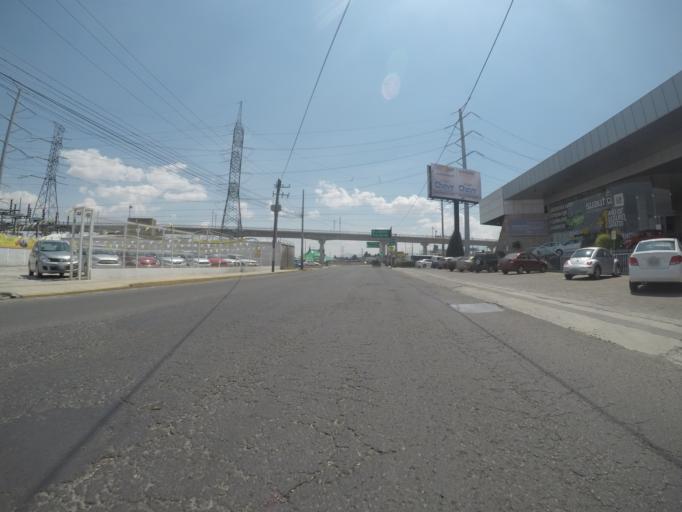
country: MX
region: Mexico
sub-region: Metepec
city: San Jorge Pueblo Nuevo
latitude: 19.2737
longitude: -99.6318
